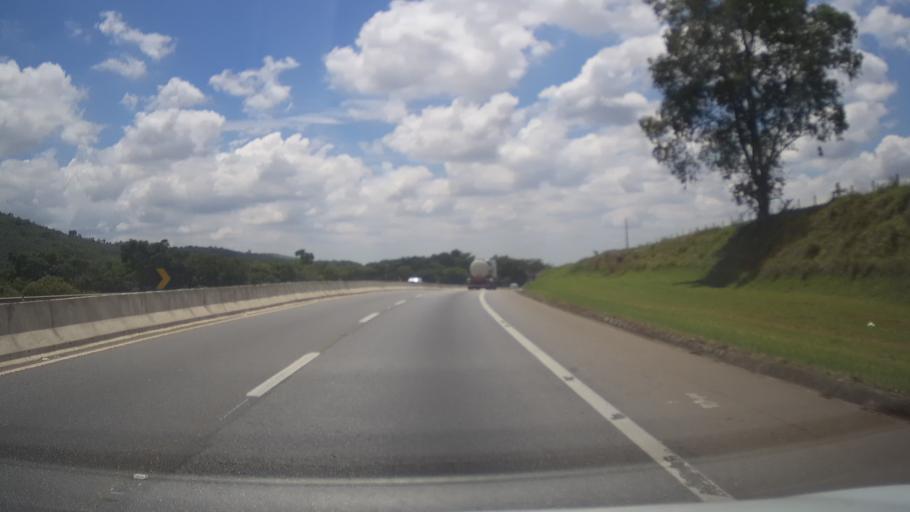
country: BR
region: Minas Gerais
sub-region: Campanha
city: Campanha
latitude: -21.8026
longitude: -45.4719
